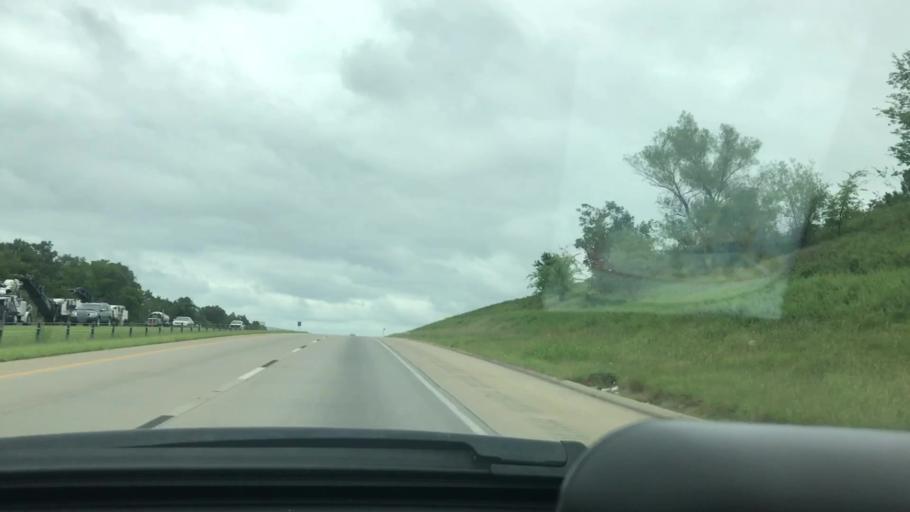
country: US
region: Oklahoma
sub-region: Pittsburg County
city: Krebs
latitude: 34.9692
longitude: -95.7238
